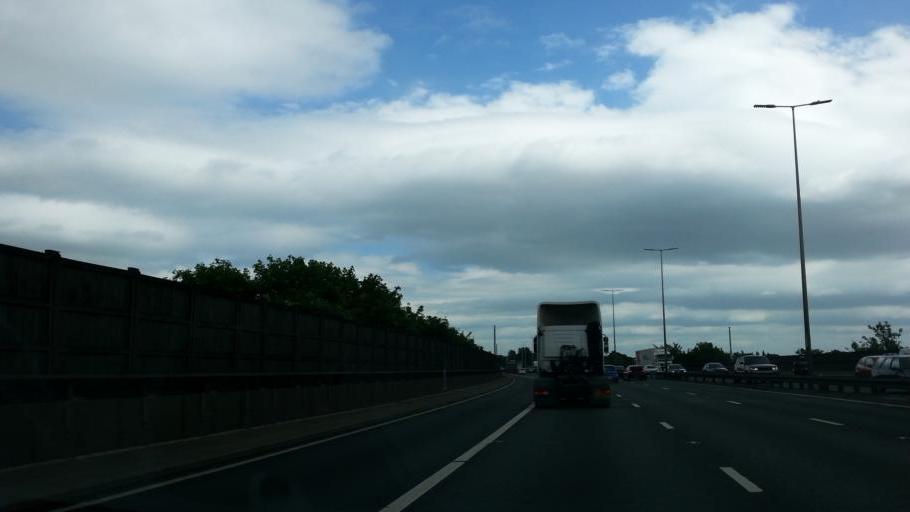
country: GB
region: England
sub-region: City and Borough of Birmingham
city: Hockley
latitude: 52.5389
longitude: -1.9094
